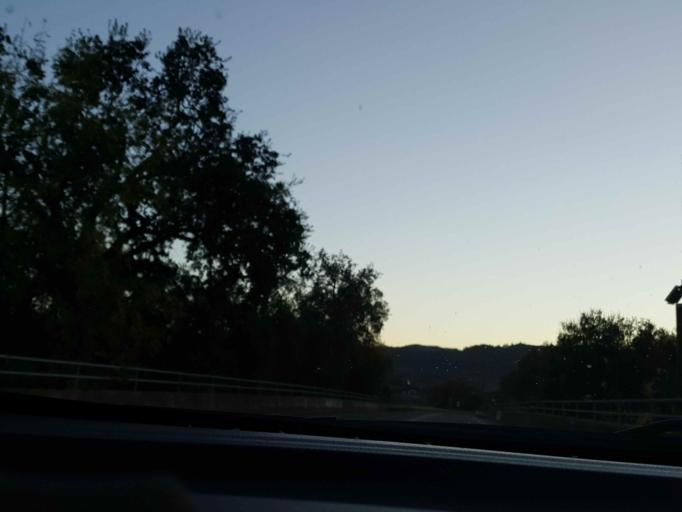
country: US
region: California
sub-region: Napa County
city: Yountville
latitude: 38.4187
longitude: -122.3513
